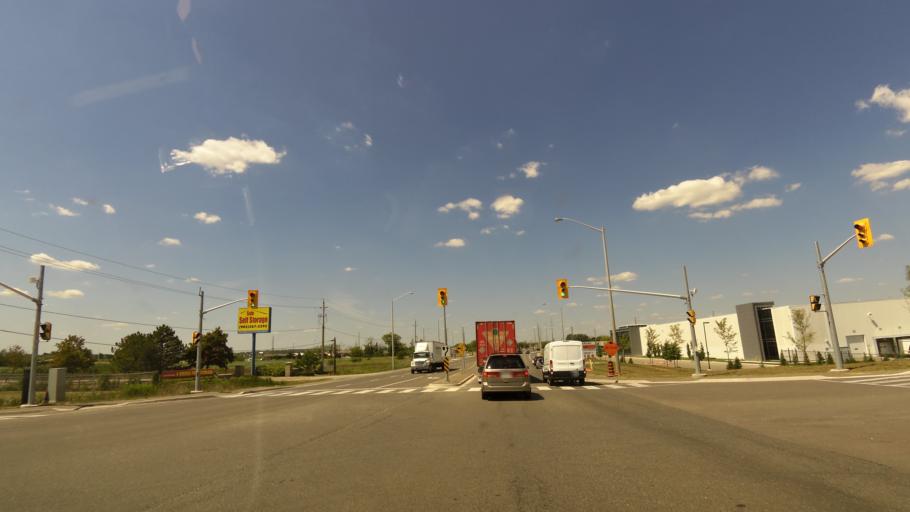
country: CA
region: Ontario
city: Brampton
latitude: 43.6059
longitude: -79.7951
